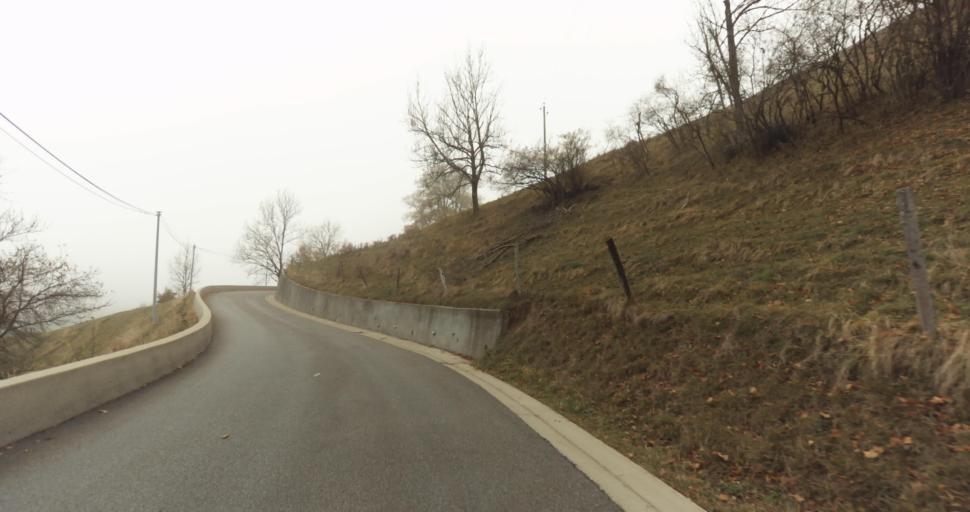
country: FR
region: Rhone-Alpes
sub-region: Departement de la Haute-Savoie
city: Doussard
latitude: 45.7980
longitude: 6.2643
